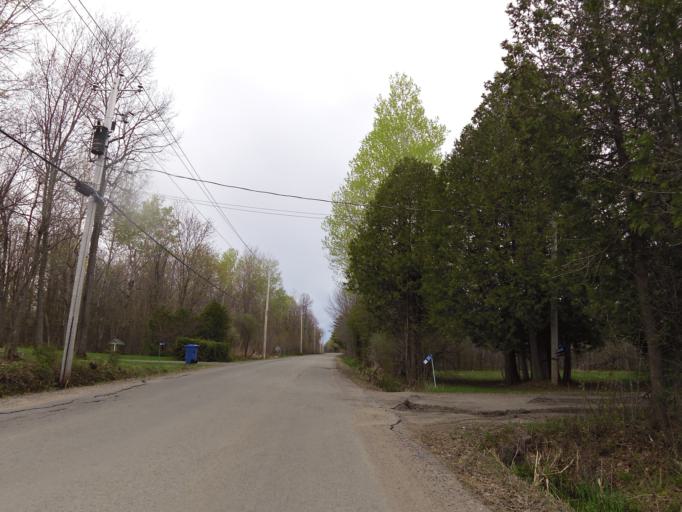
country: CA
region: Ontario
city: Hawkesbury
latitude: 45.6234
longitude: -74.5669
